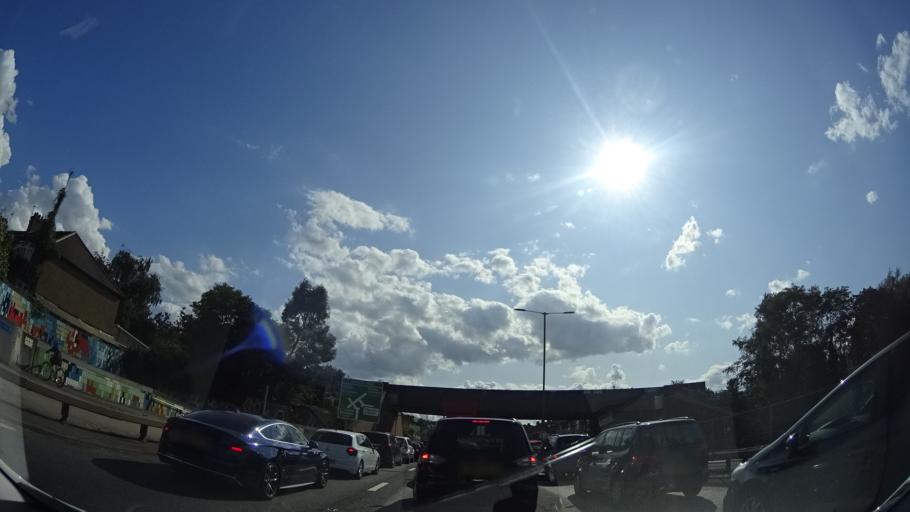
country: GB
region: England
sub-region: Greater London
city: Wembley
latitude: 51.5333
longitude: -0.2906
